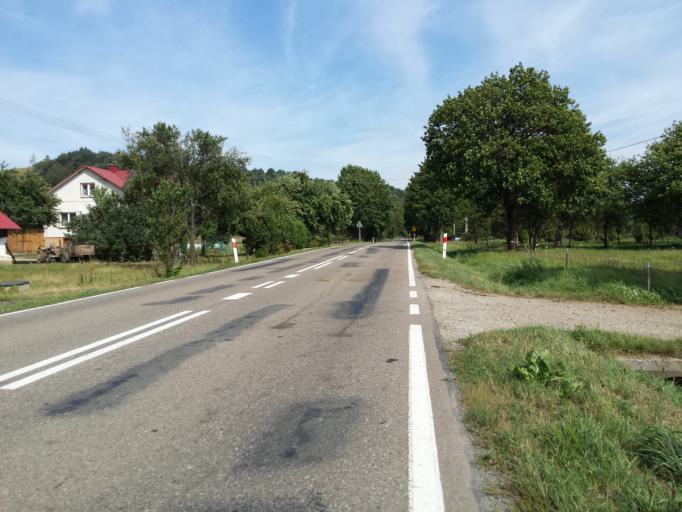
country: PL
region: Subcarpathian Voivodeship
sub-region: Powiat leski
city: Baligrod
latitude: 49.3753
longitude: 22.2759
